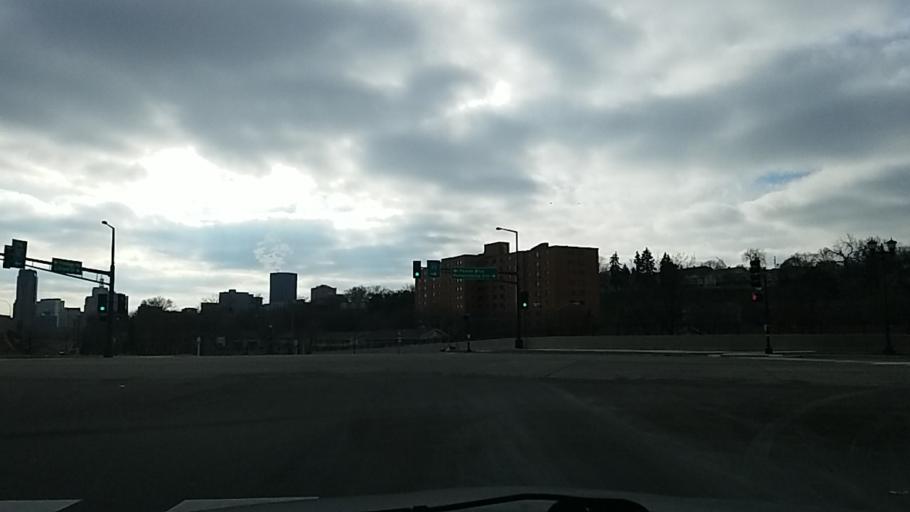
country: US
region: Minnesota
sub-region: Ramsey County
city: Saint Paul
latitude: 44.9621
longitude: -93.0915
